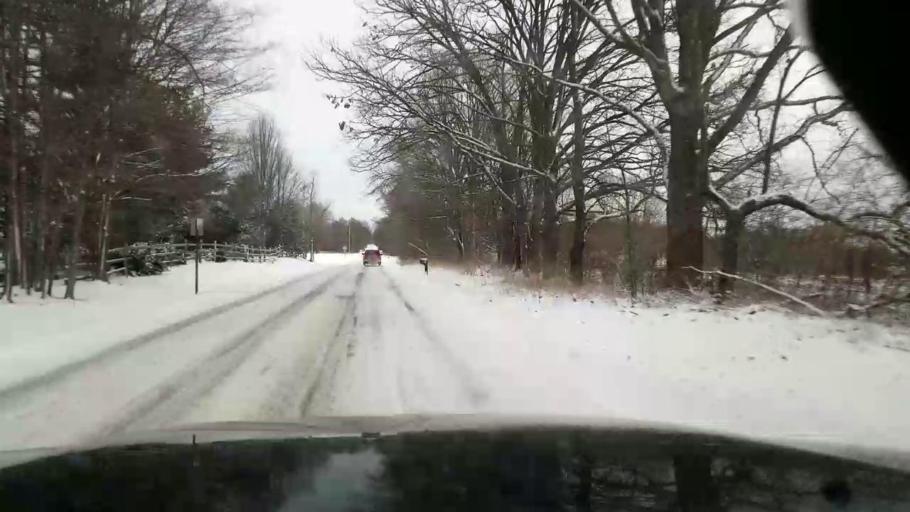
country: US
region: Michigan
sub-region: Jackson County
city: Spring Arbor
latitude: 42.1593
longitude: -84.4995
